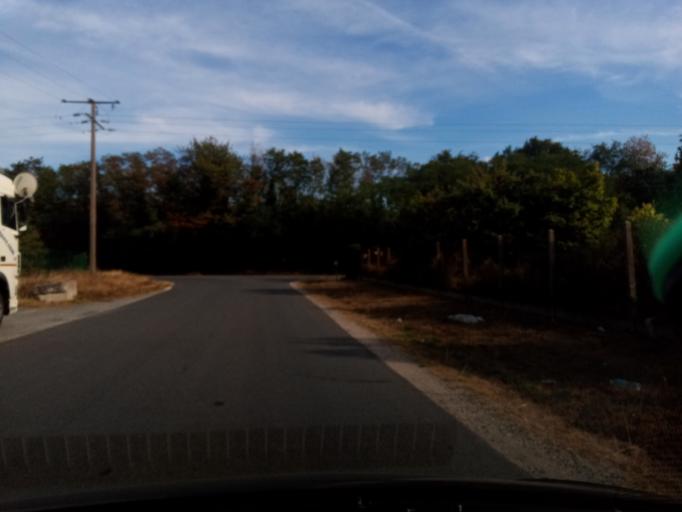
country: FR
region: Poitou-Charentes
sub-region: Departement de la Vienne
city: Saulge
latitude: 46.4015
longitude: 0.8914
